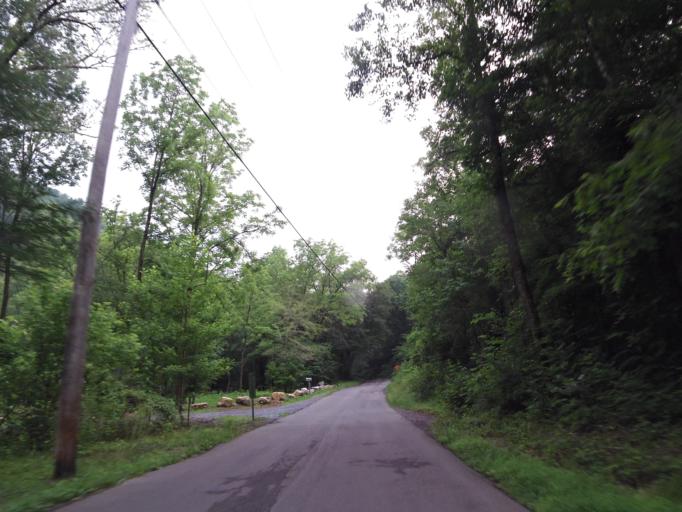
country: US
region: Tennessee
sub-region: Blount County
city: Wildwood
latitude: 35.7435
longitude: -83.7728
